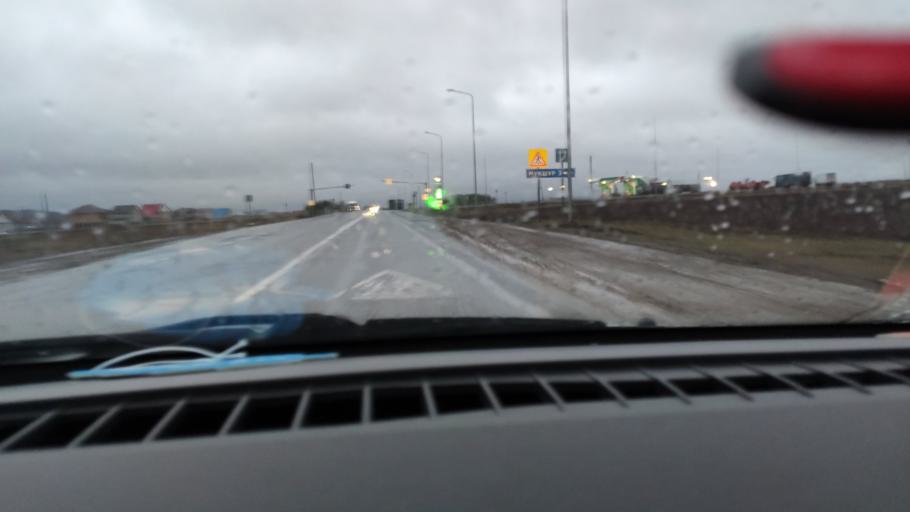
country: RU
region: Udmurtiya
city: Alnashi
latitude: 56.1723
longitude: 52.4733
